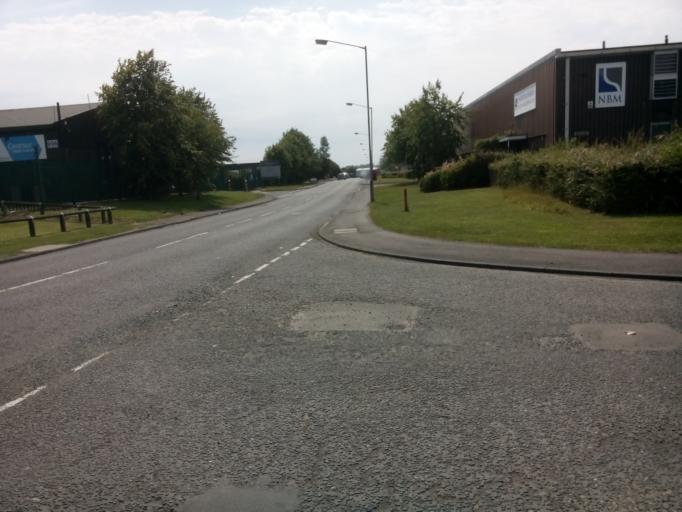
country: GB
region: England
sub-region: Northumberland
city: Backworth
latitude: 55.0215
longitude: -1.5409
